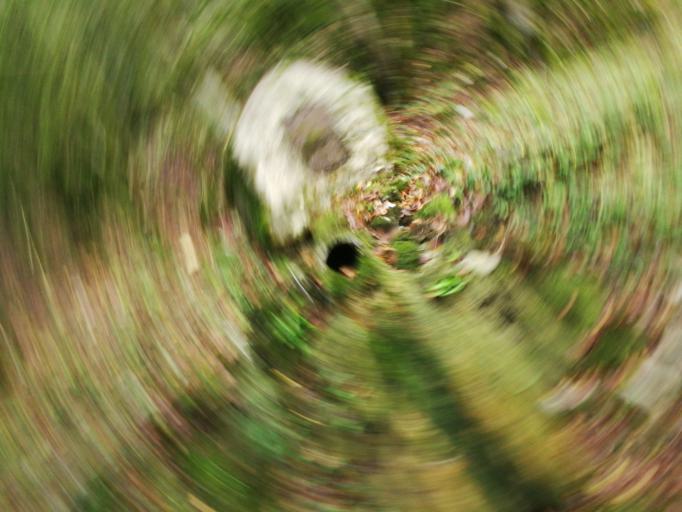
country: GE
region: Abkhazia
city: Gagra
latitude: 43.3280
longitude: 40.2615
